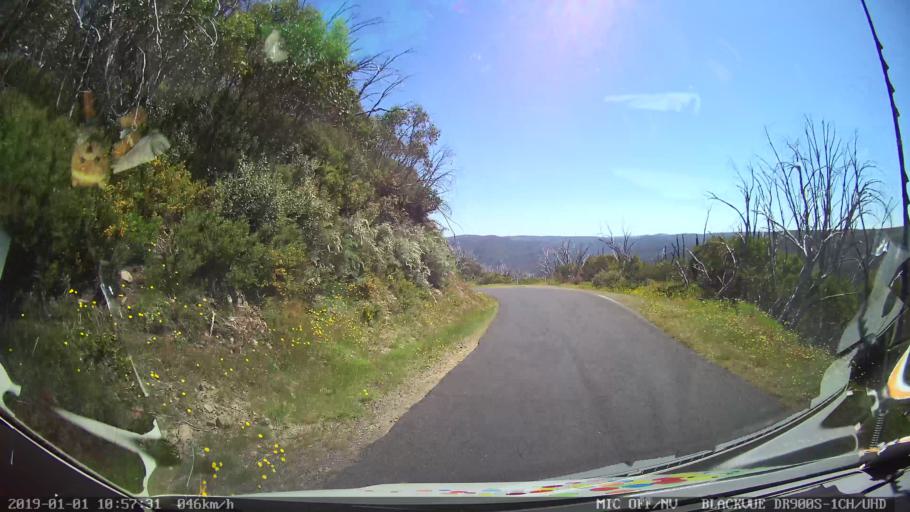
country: AU
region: New South Wales
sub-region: Snowy River
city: Jindabyne
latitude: -35.9973
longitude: 148.3966
